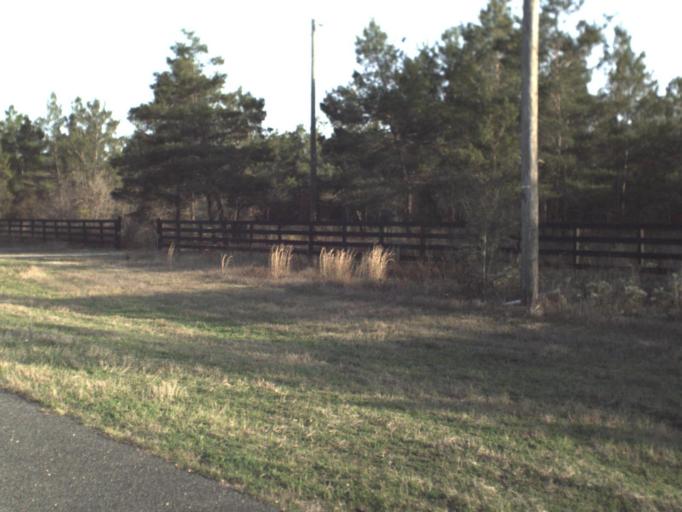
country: US
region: Florida
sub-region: Bay County
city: Lynn Haven
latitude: 30.4253
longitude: -85.6626
